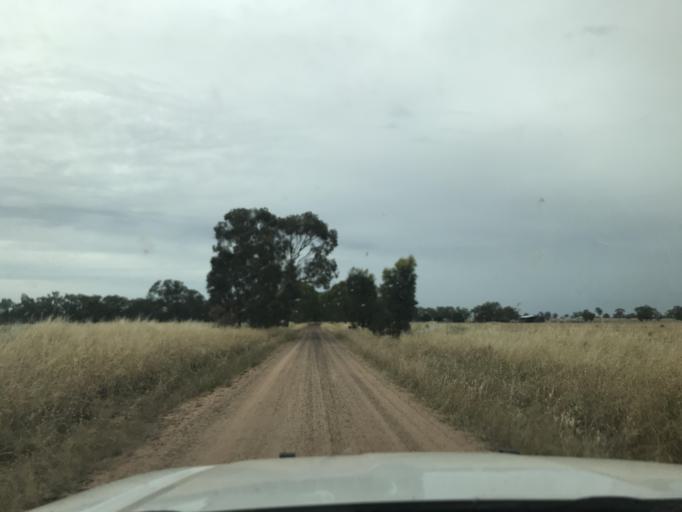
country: AU
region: Victoria
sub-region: Horsham
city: Horsham
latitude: -37.0676
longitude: 141.6656
